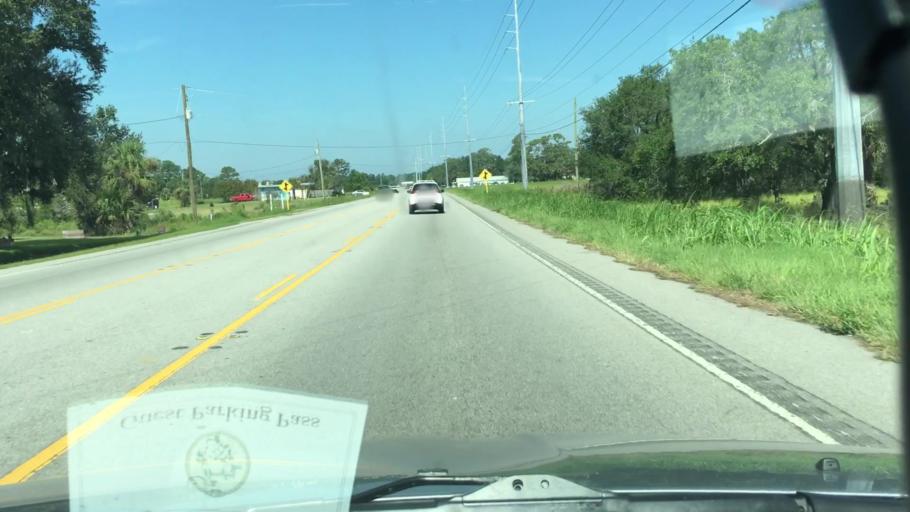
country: US
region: South Carolina
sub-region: Beaufort County
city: Beaufort
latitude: 32.3970
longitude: -80.6073
